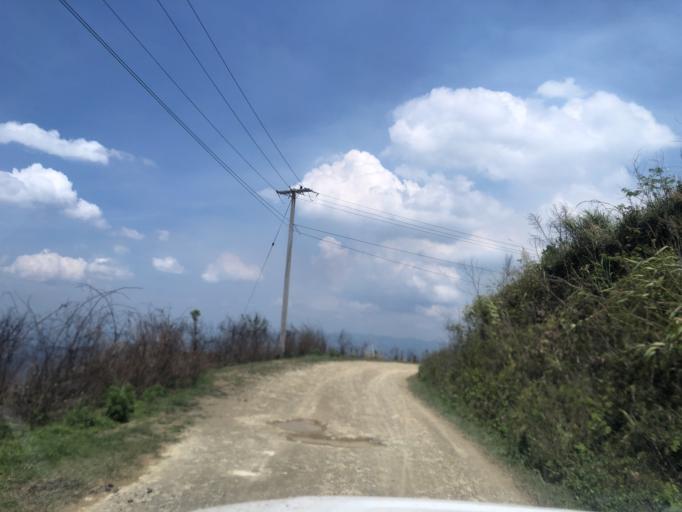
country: LA
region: Phongsali
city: Phongsali
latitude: 21.4025
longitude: 102.1883
